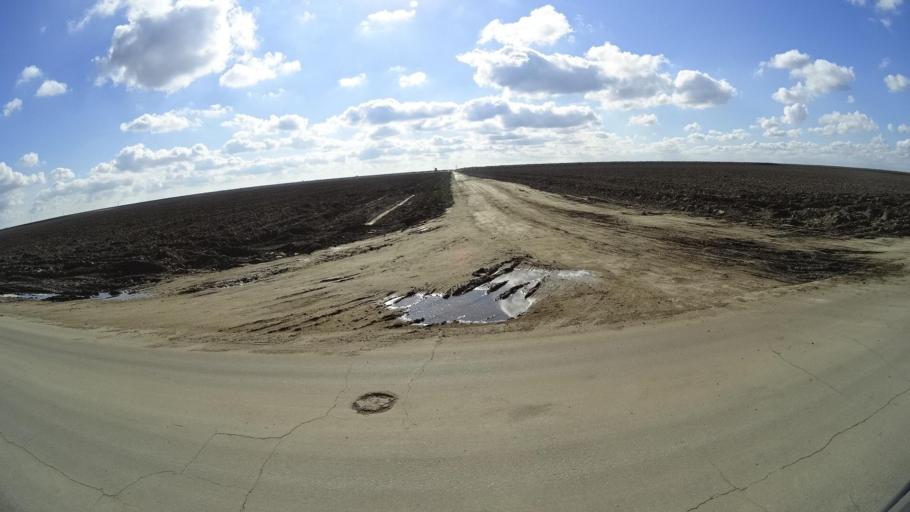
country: US
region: California
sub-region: Kern County
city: McFarland
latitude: 35.6743
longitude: -119.2853
